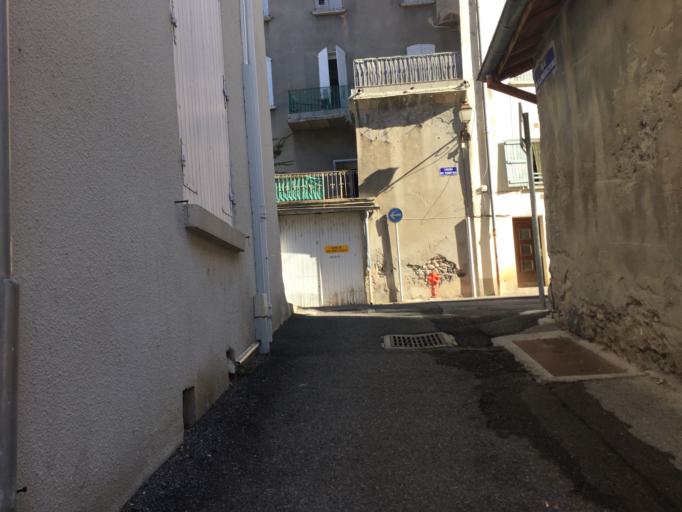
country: FR
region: Provence-Alpes-Cote d'Azur
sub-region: Departement des Alpes-de-Haute-Provence
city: Digne-les-Bains
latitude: 44.0920
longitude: 6.2385
